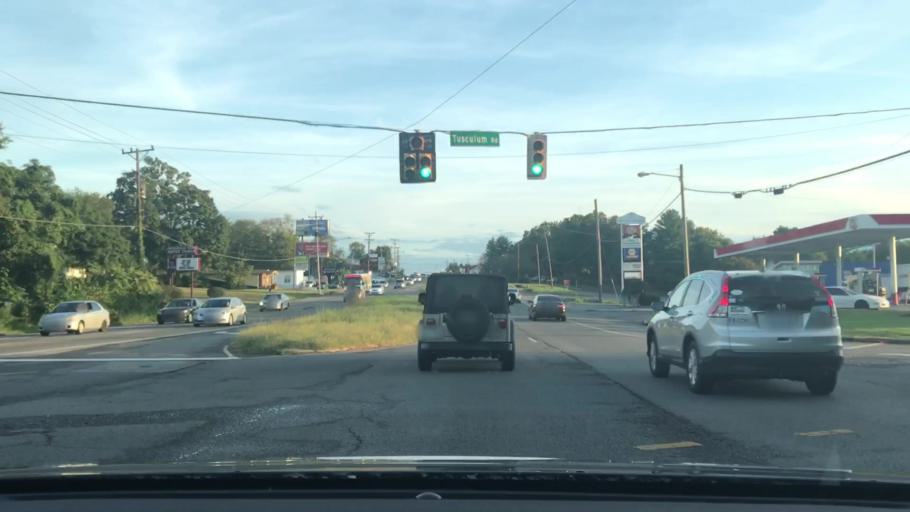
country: US
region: Tennessee
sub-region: Williamson County
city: Brentwood
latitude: 36.0591
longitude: -86.7163
